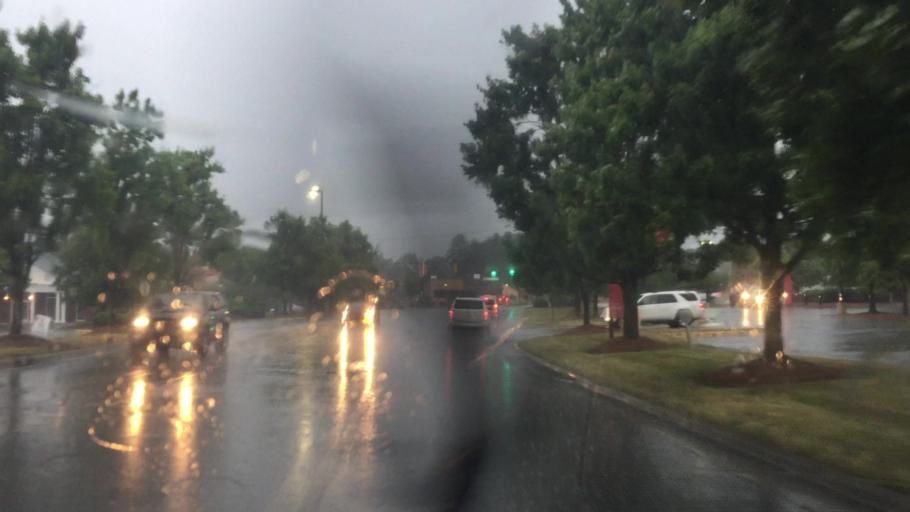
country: US
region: North Carolina
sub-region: Rowan County
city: Salisbury
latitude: 35.6520
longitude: -80.4594
